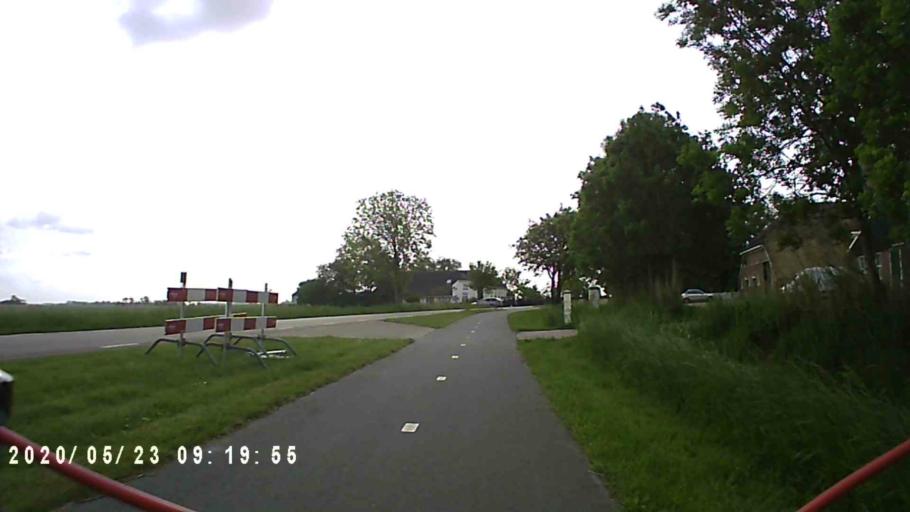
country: NL
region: Groningen
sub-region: Gemeente Bedum
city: Bedum
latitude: 53.2972
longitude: 6.6697
